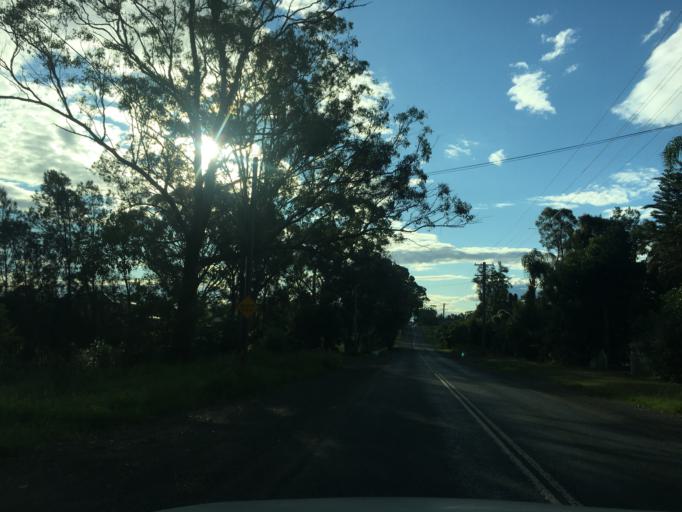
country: AU
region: New South Wales
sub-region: Campbelltown Municipality
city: Denham Court
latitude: -33.9715
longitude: 150.8031
